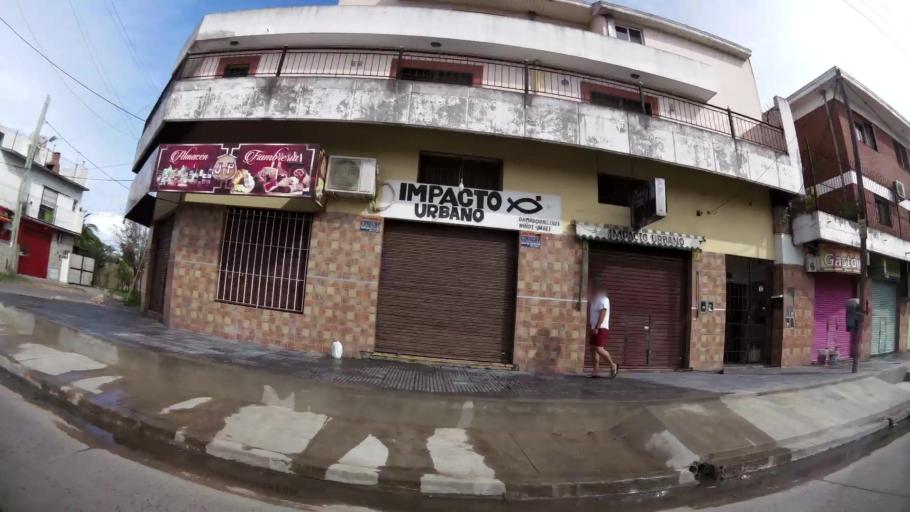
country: AR
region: Buenos Aires
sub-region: Partido de Quilmes
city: Quilmes
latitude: -34.7693
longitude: -58.2588
